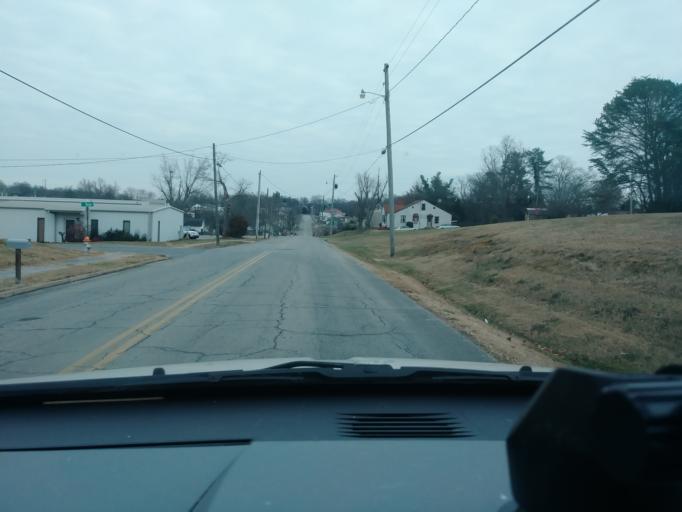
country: US
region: Tennessee
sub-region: Greene County
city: Greeneville
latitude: 36.1546
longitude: -82.8459
